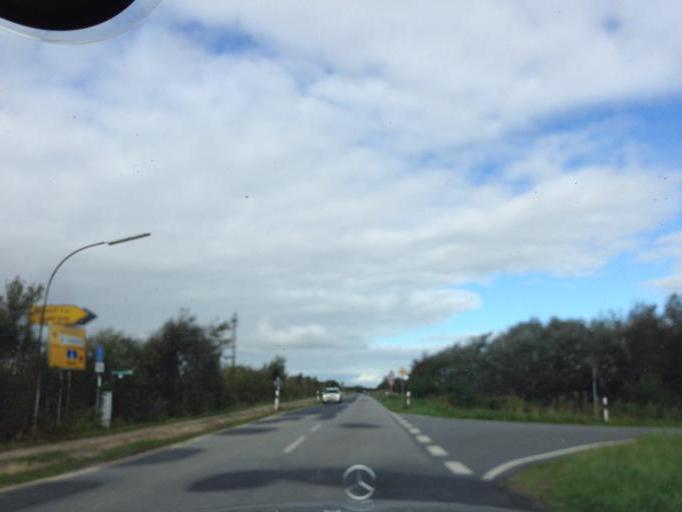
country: DE
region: Schleswig-Holstein
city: Dagebull
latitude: 54.7321
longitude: 8.7133
